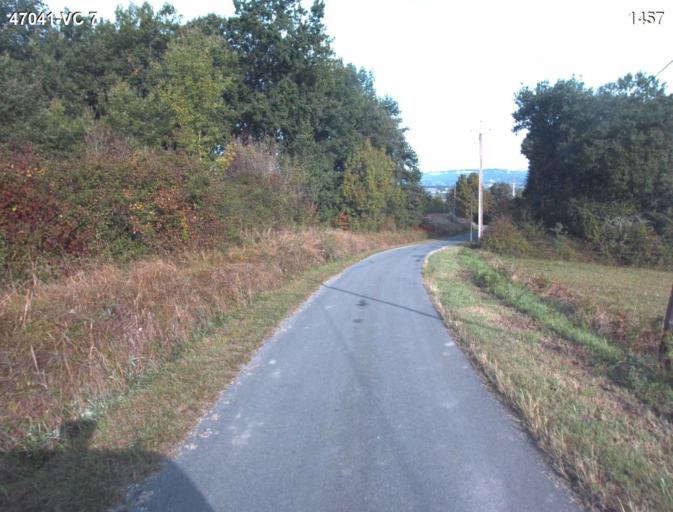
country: FR
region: Aquitaine
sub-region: Departement du Lot-et-Garonne
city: Port-Sainte-Marie
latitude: 44.1969
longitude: 0.4164
